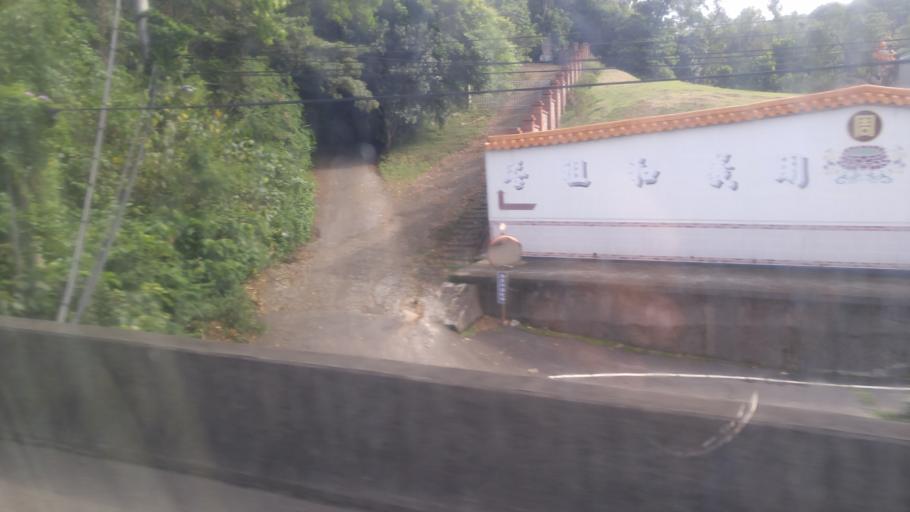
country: TW
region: Taiwan
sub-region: Hsinchu
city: Zhubei
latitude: 24.8931
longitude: 121.1068
